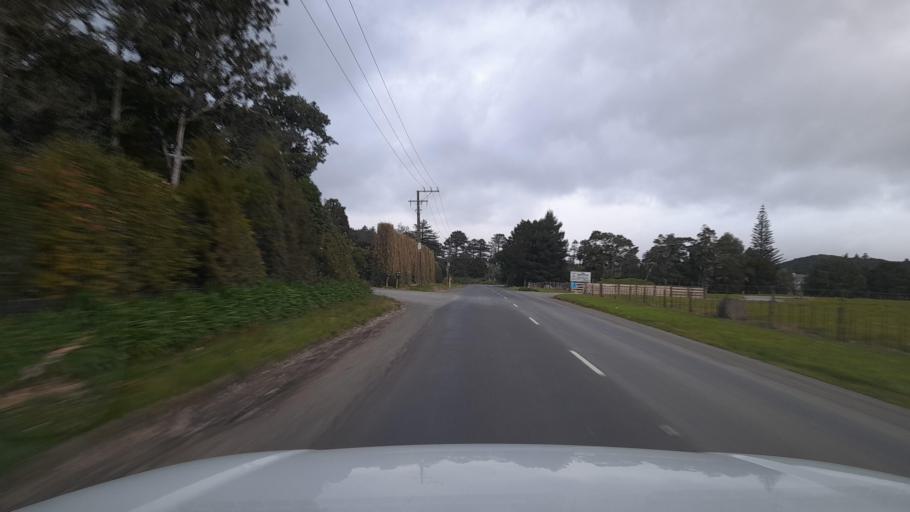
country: NZ
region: Northland
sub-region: Whangarei
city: Maungatapere
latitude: -35.7464
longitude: 174.2107
